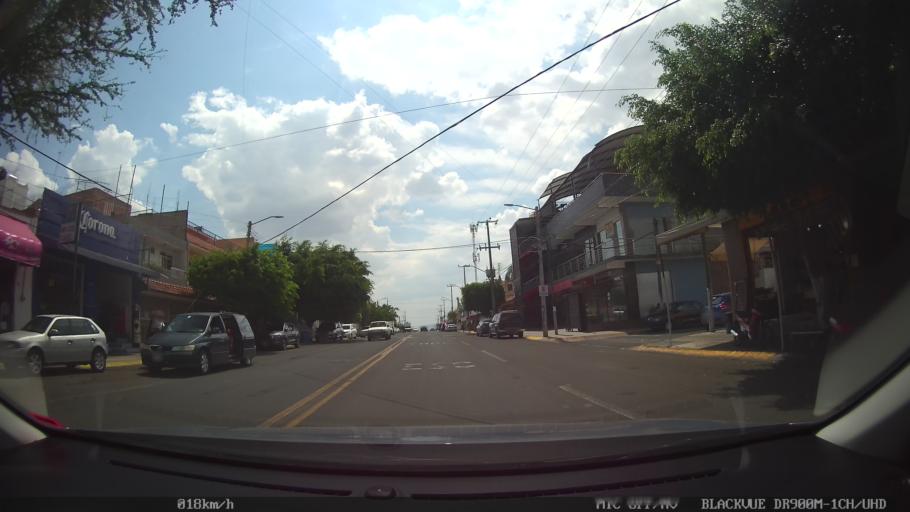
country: MX
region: Jalisco
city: Tonala
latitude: 20.6243
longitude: -103.2570
